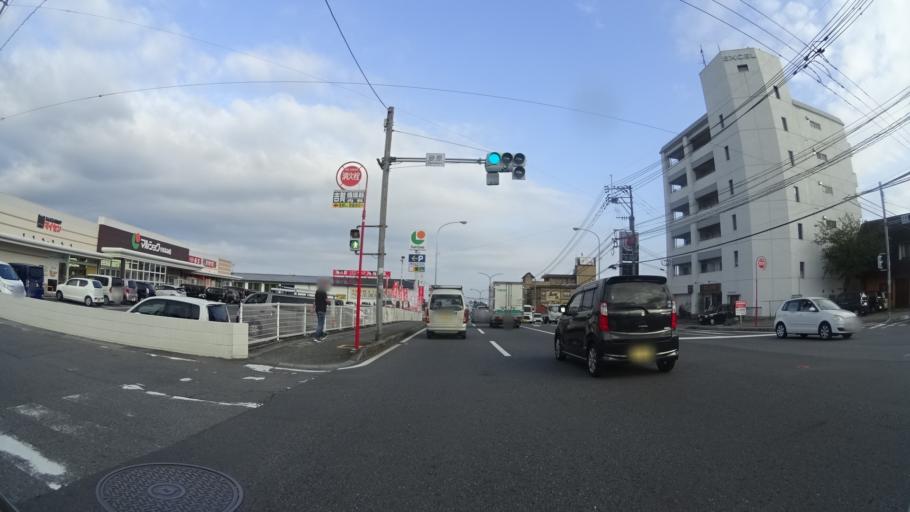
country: JP
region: Oita
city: Beppu
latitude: 33.3131
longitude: 131.4792
